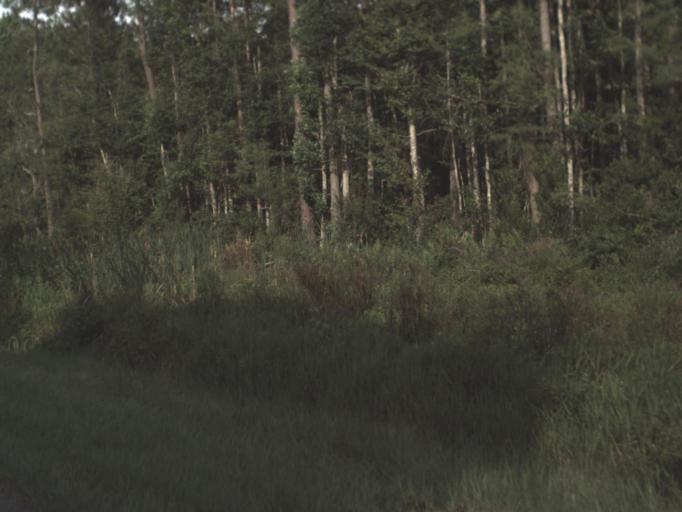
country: US
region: Florida
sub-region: Madison County
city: Madison
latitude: 30.4143
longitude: -83.6391
